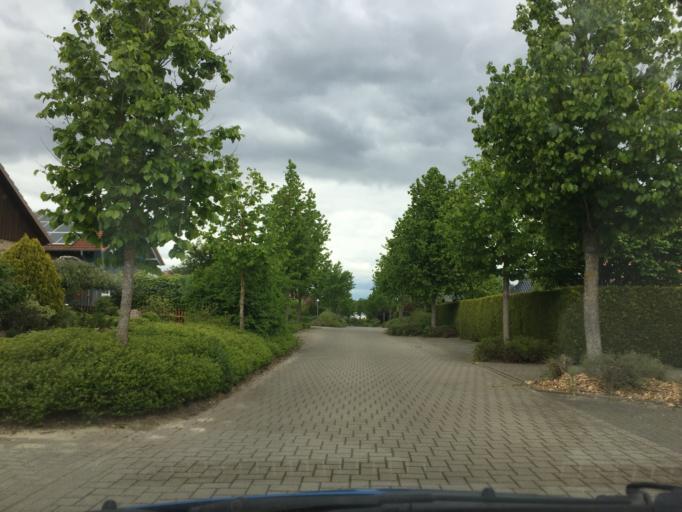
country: DE
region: Lower Saxony
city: Uelzen
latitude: 52.9263
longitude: 10.5222
